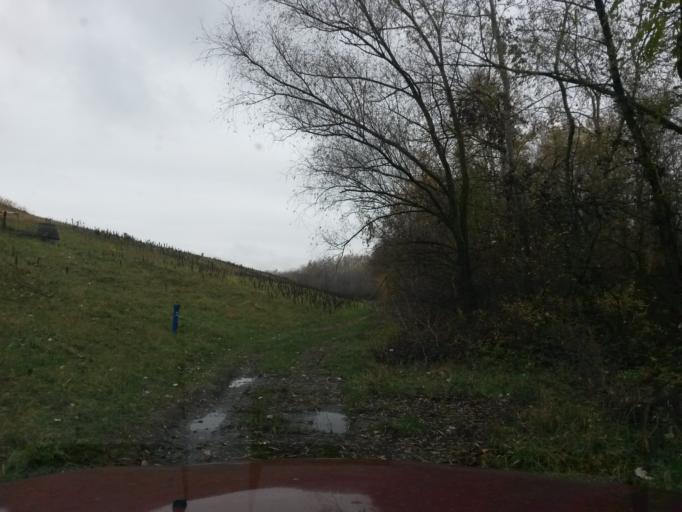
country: SK
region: Kosicky
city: Cierna nad Tisou
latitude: 48.5611
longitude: 21.9844
